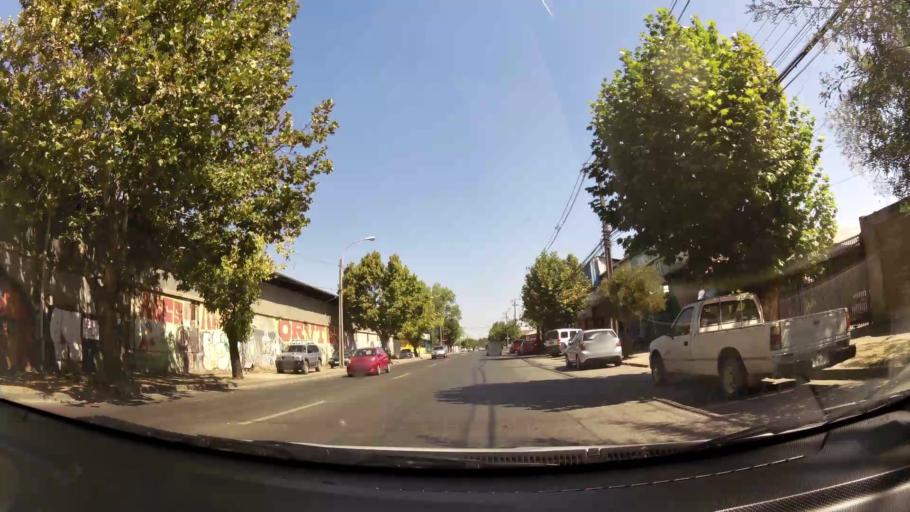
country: CL
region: Maule
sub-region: Provincia de Talca
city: Talca
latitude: -35.4324
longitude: -71.6508
